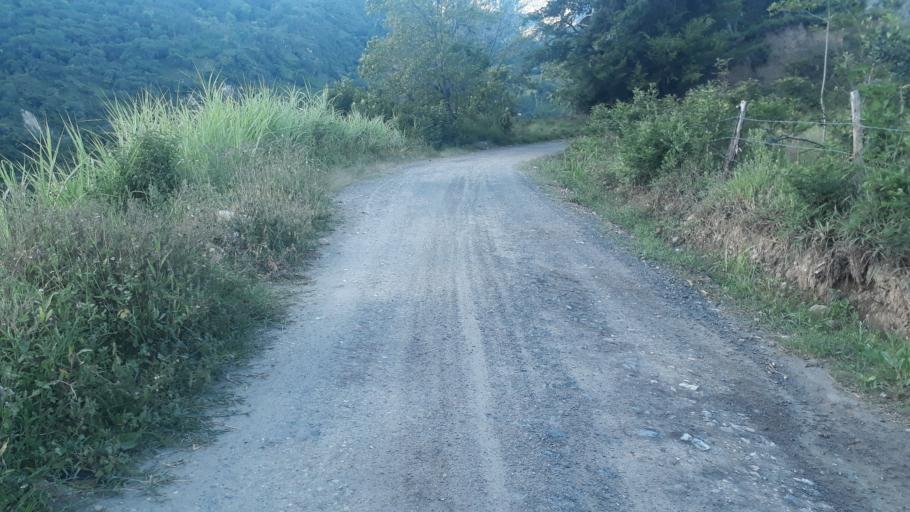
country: CO
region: Boyaca
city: San Mateo
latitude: 6.4014
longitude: -72.5585
